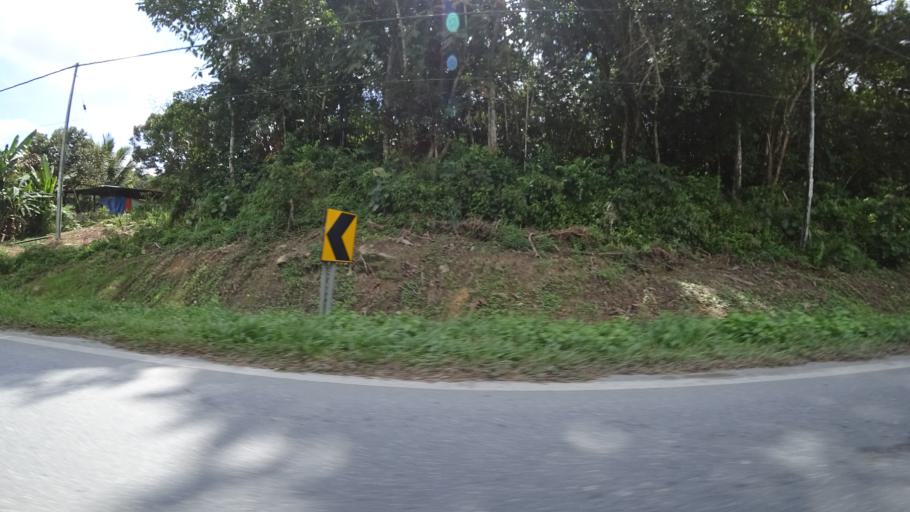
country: MY
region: Sarawak
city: Limbang
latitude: 4.6566
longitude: 114.9718
